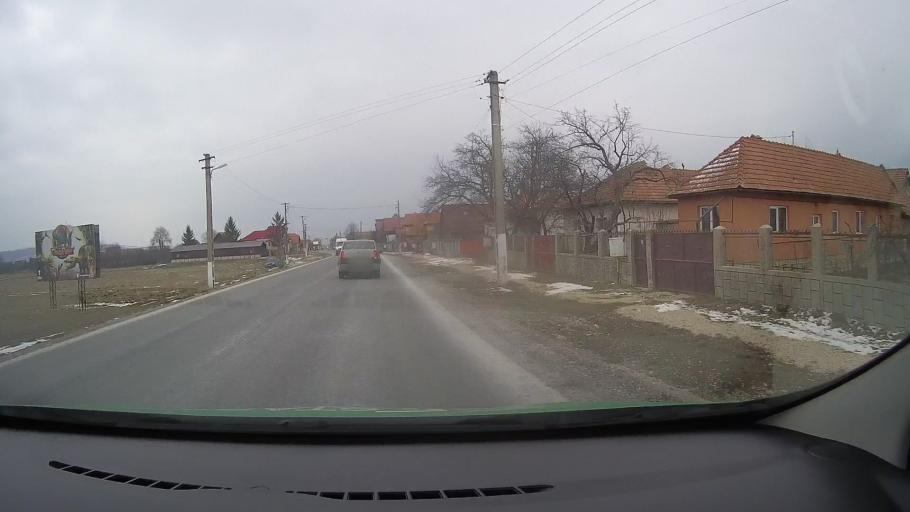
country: RO
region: Brasov
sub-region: Comuna Zarnesti
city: Tohanu Nou
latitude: 45.5482
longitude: 25.3845
